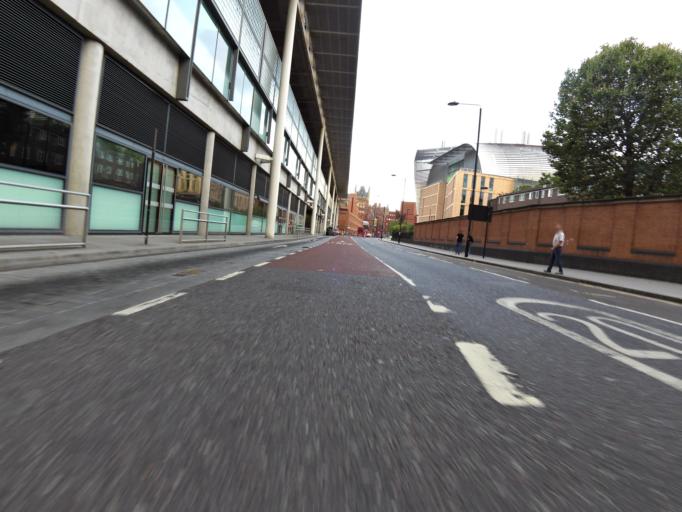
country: GB
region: England
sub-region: Greater London
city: Barnsbury
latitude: 51.5332
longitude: -0.1285
